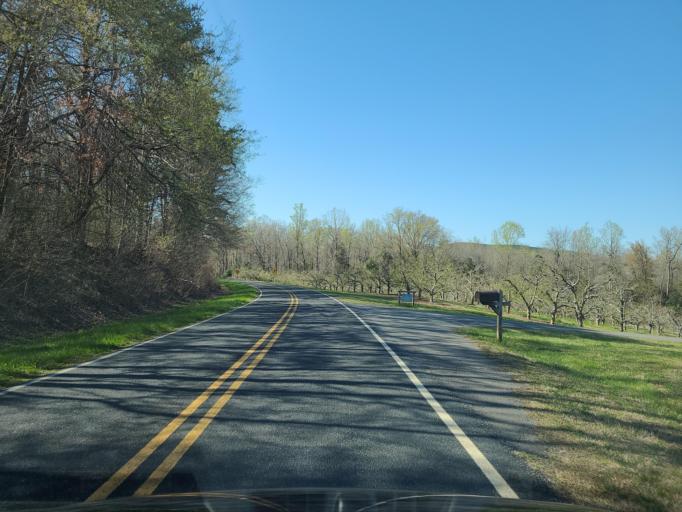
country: US
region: North Carolina
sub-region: Gaston County
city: Cherryville
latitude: 35.5264
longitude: -81.5048
